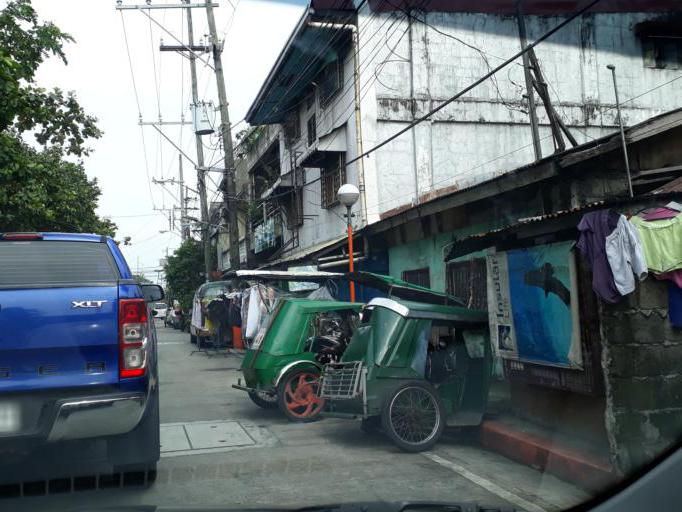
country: PH
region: Metro Manila
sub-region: City of Manila
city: Manila
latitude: 14.6223
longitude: 120.9841
